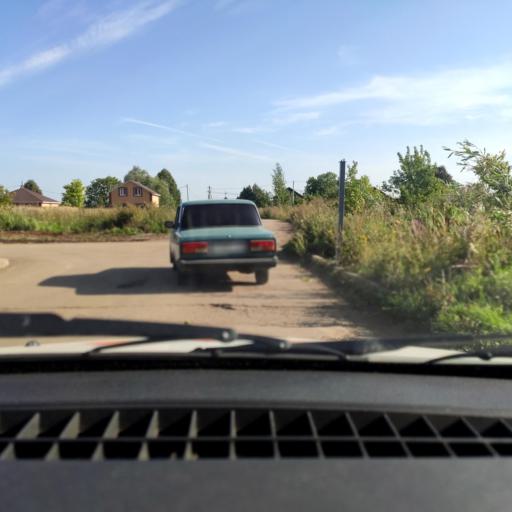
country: RU
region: Bashkortostan
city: Kabakovo
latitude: 54.6252
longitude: 56.1322
